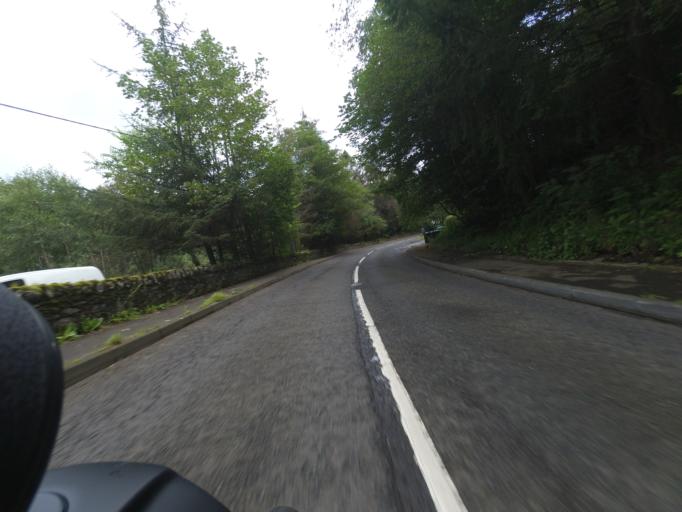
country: GB
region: Scotland
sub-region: Perth and Kinross
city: Blairgowrie
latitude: 56.6081
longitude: -3.3470
